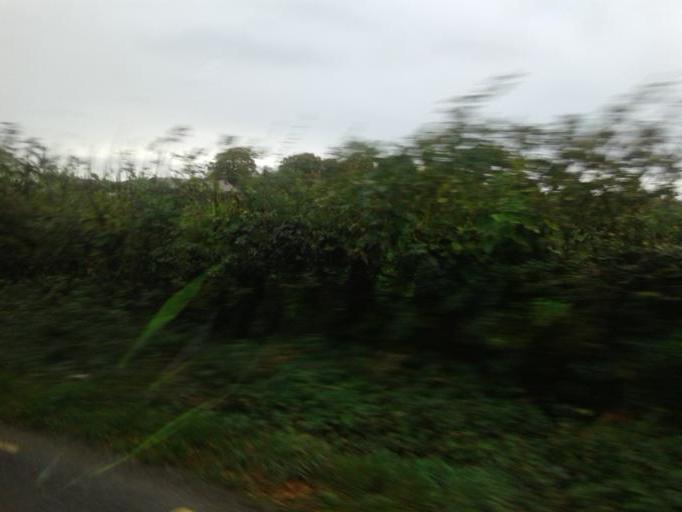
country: IE
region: Munster
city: Nenagh Bridge
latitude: 52.9277
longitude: -8.0462
